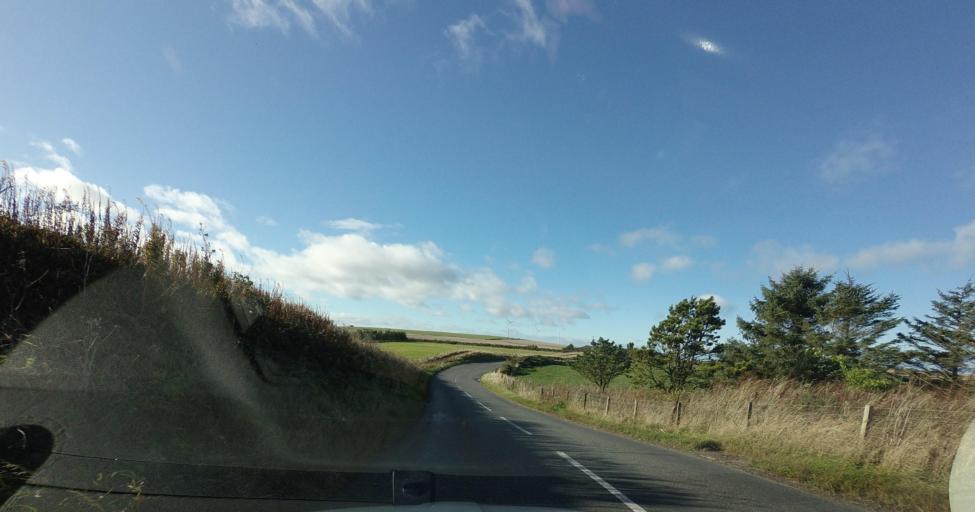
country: GB
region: Scotland
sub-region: Aberdeenshire
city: Macduff
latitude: 57.6593
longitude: -2.3477
